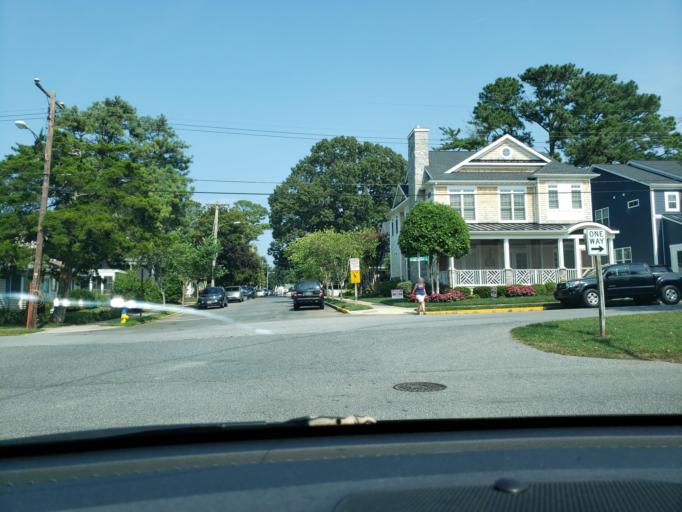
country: US
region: Delaware
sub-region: Sussex County
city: Rehoboth Beach
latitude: 38.7134
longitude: -75.0849
